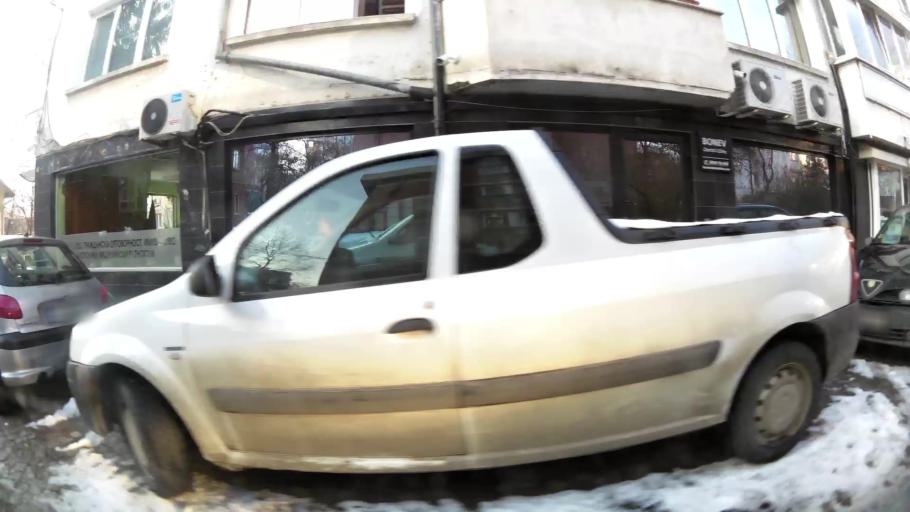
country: BG
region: Sofia-Capital
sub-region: Stolichna Obshtina
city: Sofia
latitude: 42.6853
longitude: 23.3542
